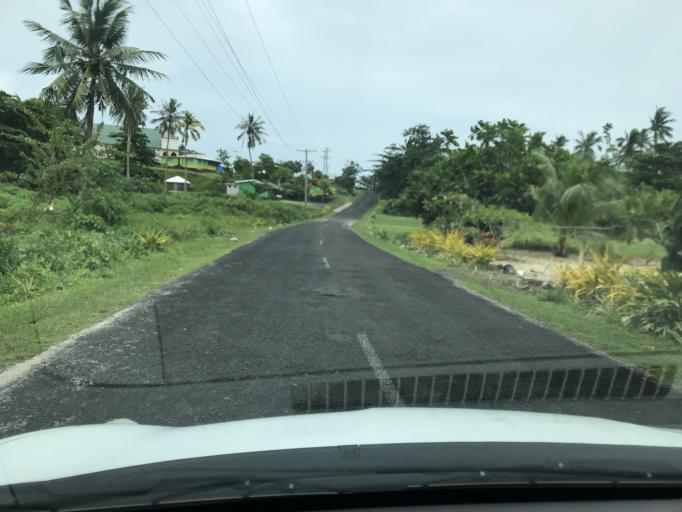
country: WS
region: Va`a-o-Fonoti
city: Samamea
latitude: -14.0466
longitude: -171.4405
